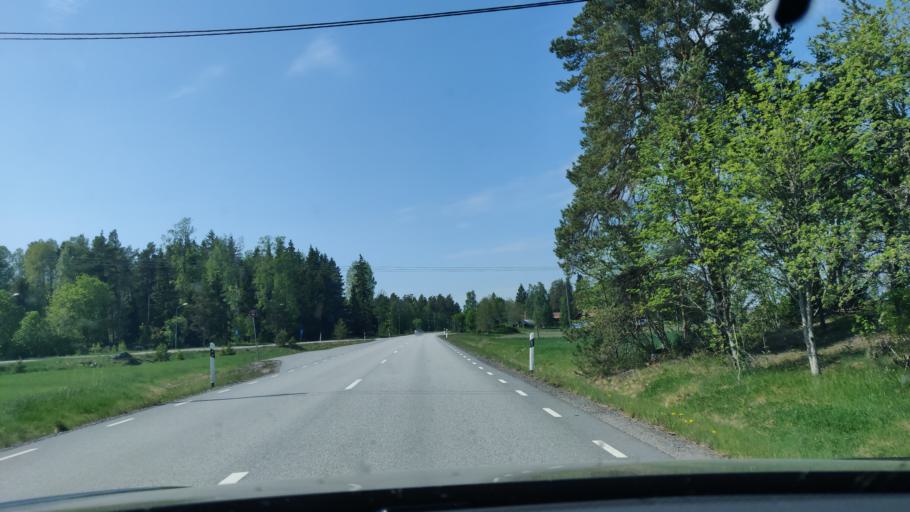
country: SE
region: Uppsala
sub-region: Heby Kommun
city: OEstervala
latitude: 60.1655
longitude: 17.1952
